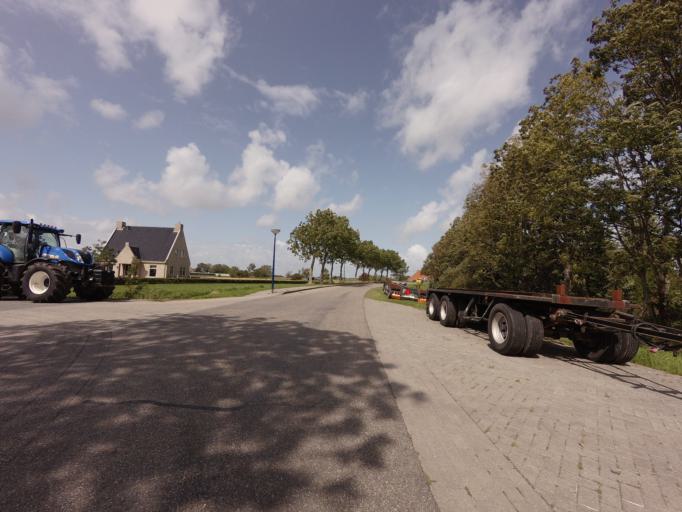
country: NL
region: Friesland
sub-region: Gemeente Harlingen
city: Harlingen
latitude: 53.1494
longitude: 5.4772
